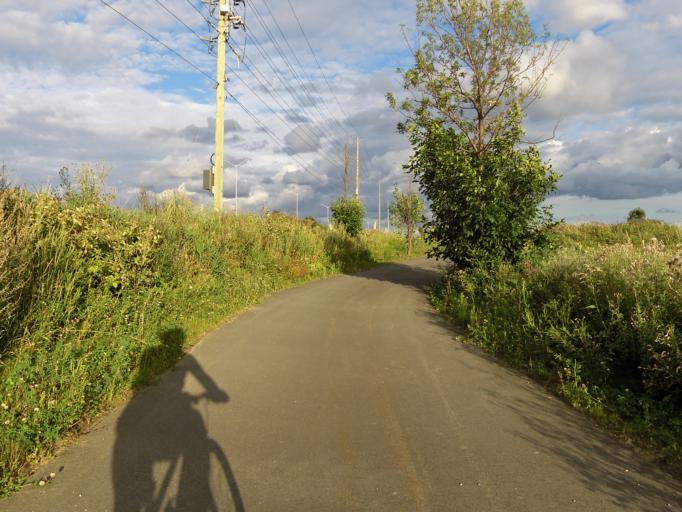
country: CA
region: Ontario
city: Bells Corners
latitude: 45.3122
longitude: -75.9351
